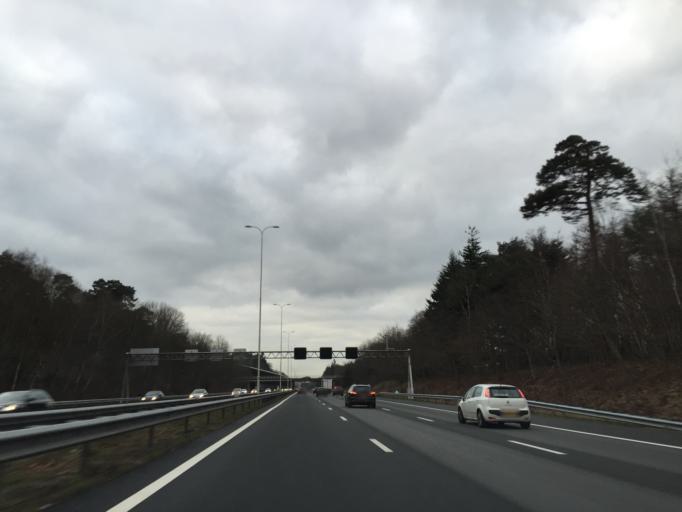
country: NL
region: Utrecht
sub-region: Gemeente Zeist
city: Zeist
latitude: 52.1044
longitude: 5.2433
